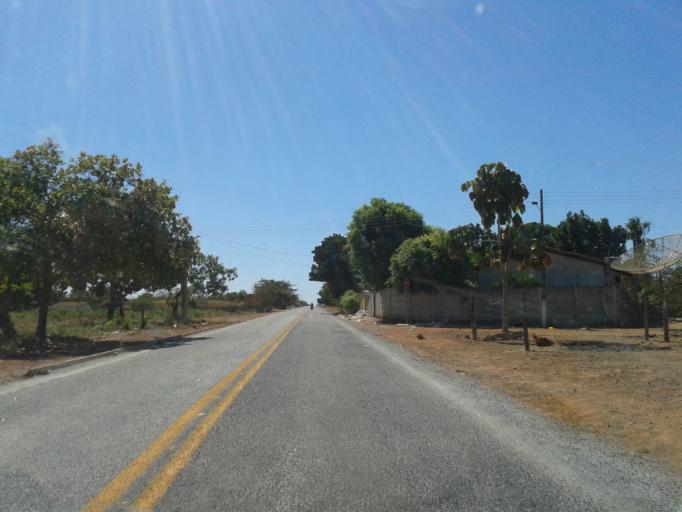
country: BR
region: Goias
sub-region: Sao Miguel Do Araguaia
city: Sao Miguel do Araguaia
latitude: -13.2641
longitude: -50.1496
